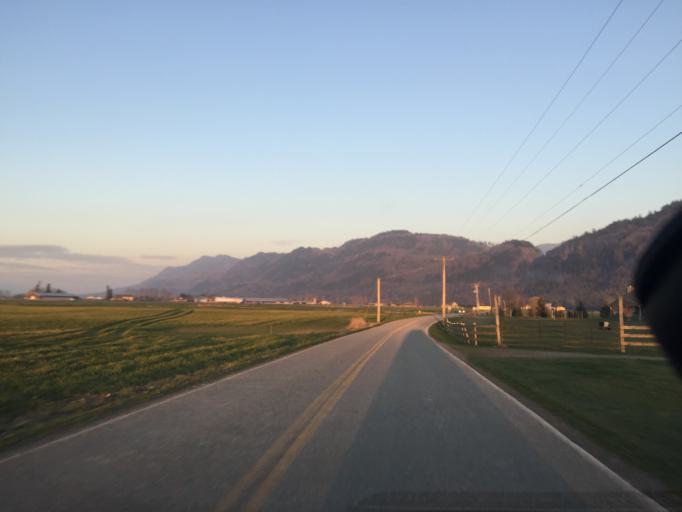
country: US
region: Washington
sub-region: Whatcom County
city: Peaceful Valley
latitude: 48.9998
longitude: -122.1889
